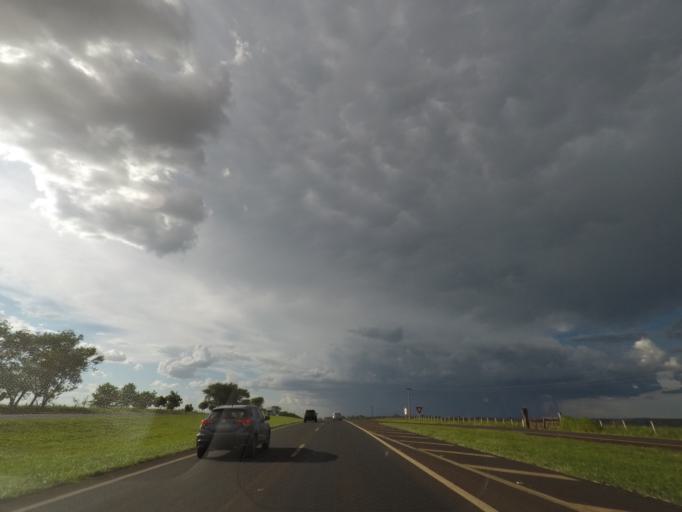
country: BR
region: Sao Paulo
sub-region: Jardinopolis
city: Jardinopolis
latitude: -21.0817
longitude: -47.8024
